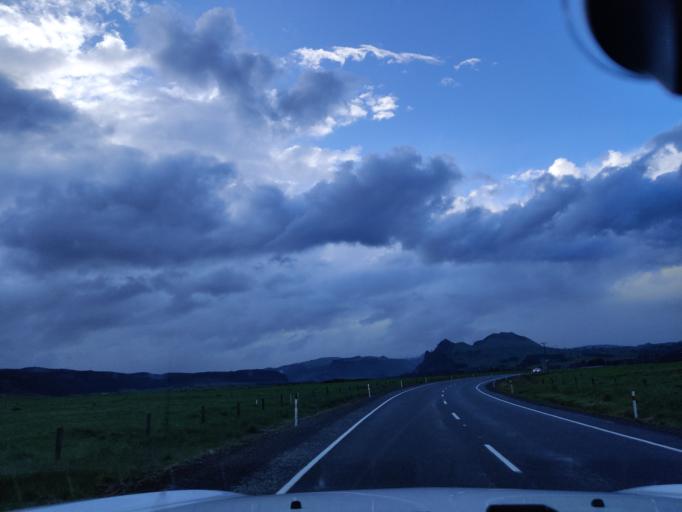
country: NZ
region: Waikato
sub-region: South Waikato District
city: Tokoroa
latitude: -38.3991
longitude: 175.7882
